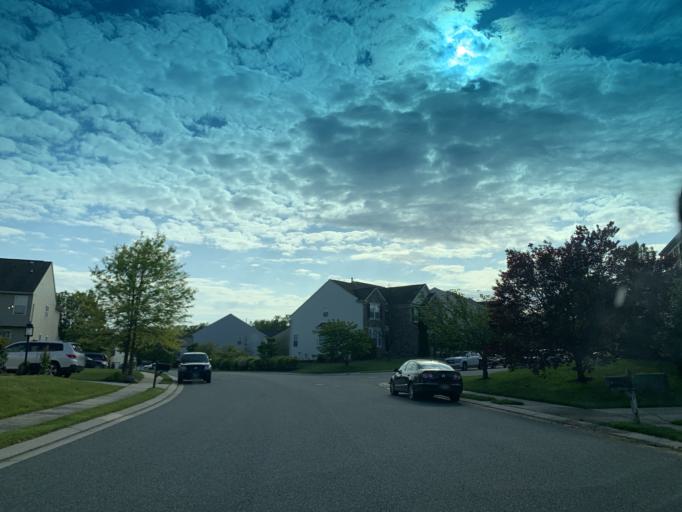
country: US
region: Maryland
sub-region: Baltimore County
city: White Marsh
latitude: 39.4032
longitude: -76.4287
